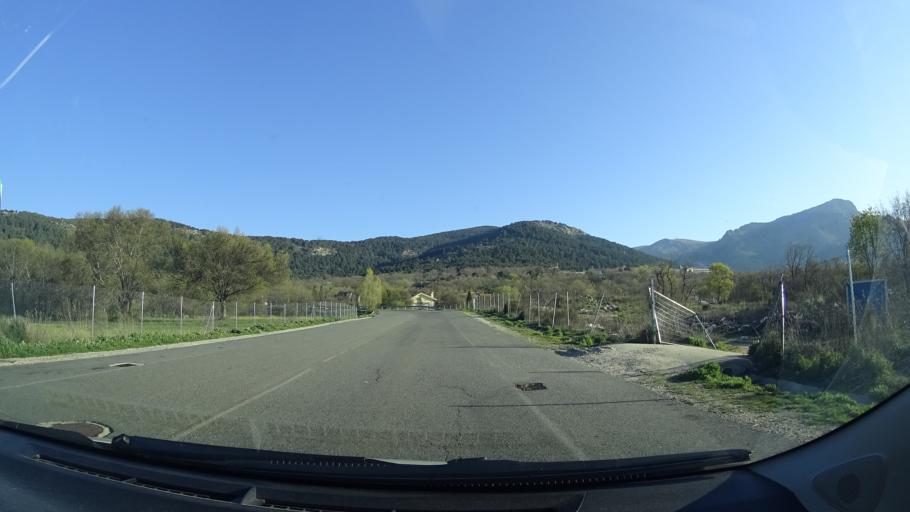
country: ES
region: Madrid
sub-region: Provincia de Madrid
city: Navacerrada
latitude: 40.7352
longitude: -4.0059
